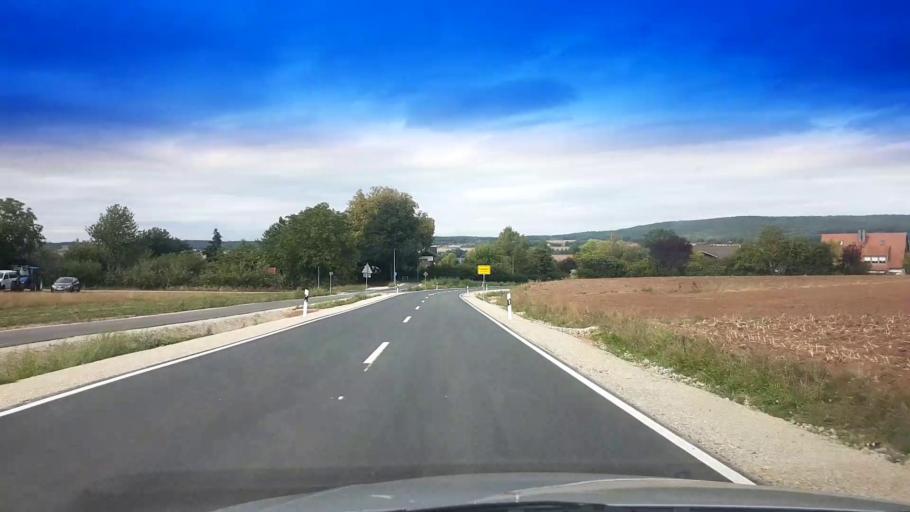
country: DE
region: Bavaria
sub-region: Upper Franconia
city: Frensdorf
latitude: 49.8114
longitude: 10.8709
